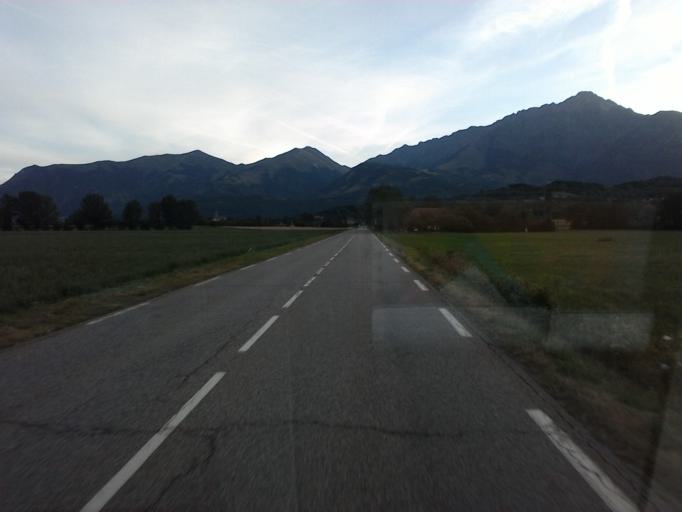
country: FR
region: Provence-Alpes-Cote d'Azur
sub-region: Departement des Hautes-Alpes
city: Saint-Bonnet-en-Champsaur
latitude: 44.7457
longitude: 6.0079
